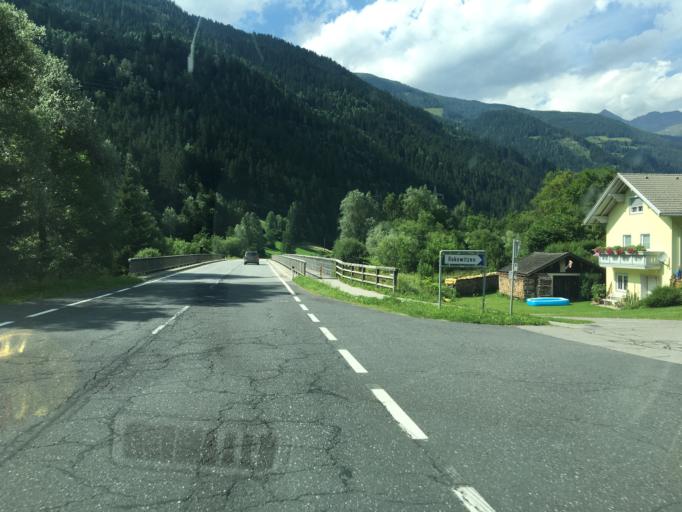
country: AT
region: Carinthia
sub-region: Politischer Bezirk Spittal an der Drau
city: Stall
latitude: 46.9046
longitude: 13.0682
